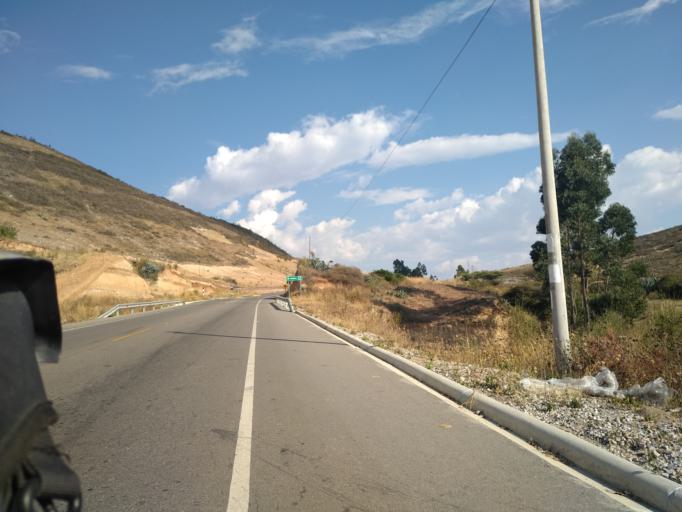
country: PE
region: Cajamarca
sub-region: San Marcos
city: San Marcos
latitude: -7.3784
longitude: -78.1266
